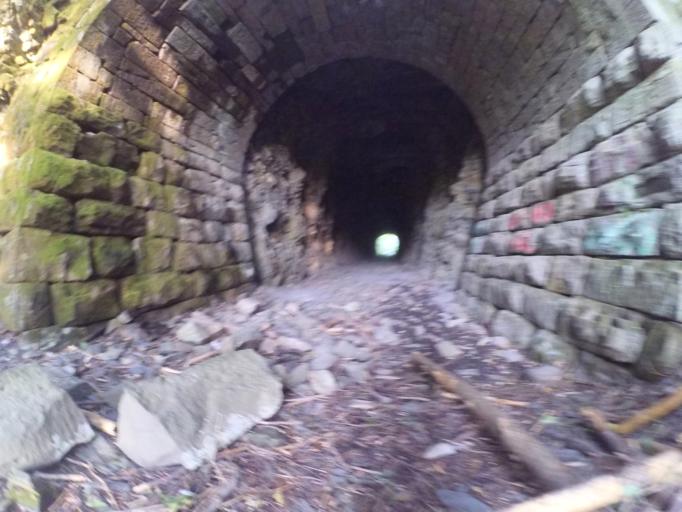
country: US
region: Pennsylvania
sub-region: Mifflin County
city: Milroy
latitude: 40.8490
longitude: -77.4524
